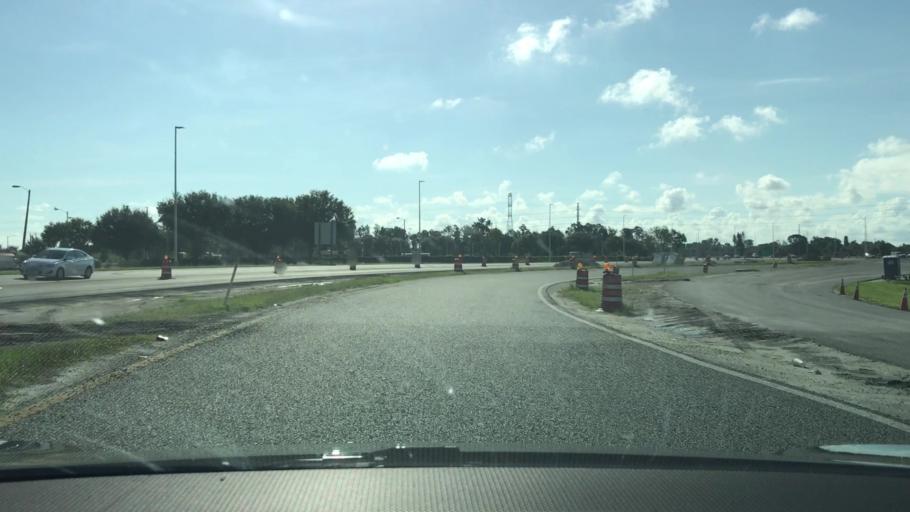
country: US
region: Florida
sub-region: Orange County
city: Williamsburg
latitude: 28.4226
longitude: -81.4584
